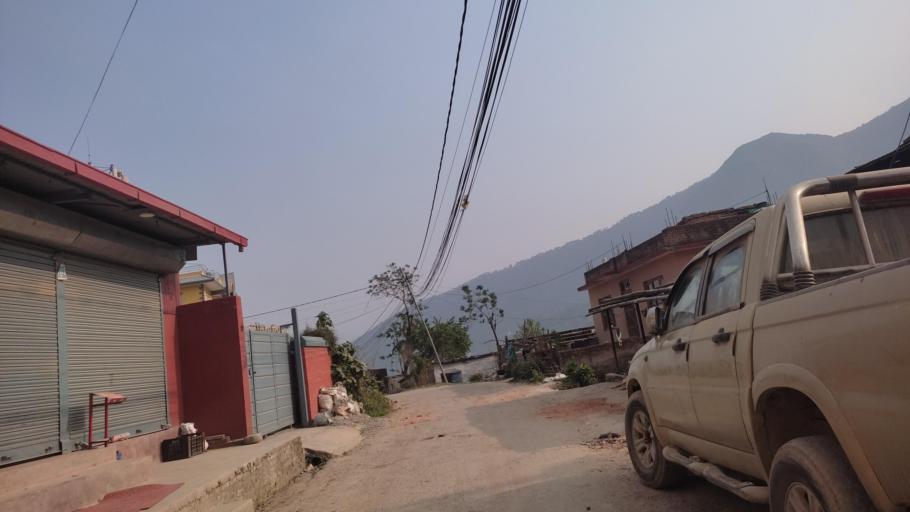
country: NP
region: Central Region
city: Kirtipur
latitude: 27.6622
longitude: 85.2779
